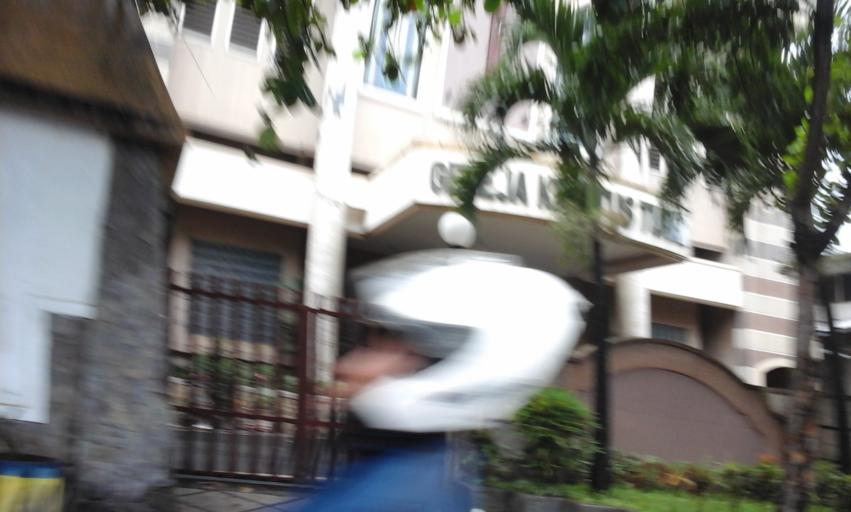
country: ID
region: East Java
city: Kadipaten
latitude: -8.1303
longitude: 113.2190
